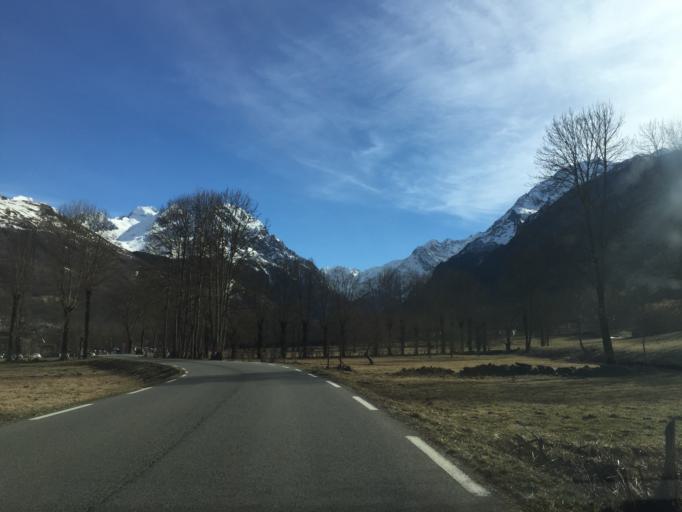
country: FR
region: Midi-Pyrenees
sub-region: Departement des Hautes-Pyrenees
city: Saint-Lary-Soulan
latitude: 42.8004
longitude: 0.4050
